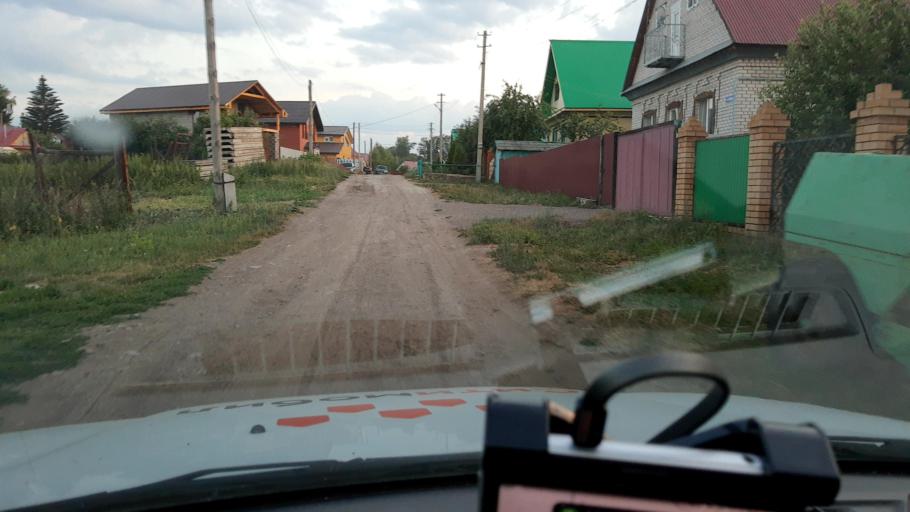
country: RU
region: Bashkortostan
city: Mikhaylovka
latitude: 54.8657
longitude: 55.8140
